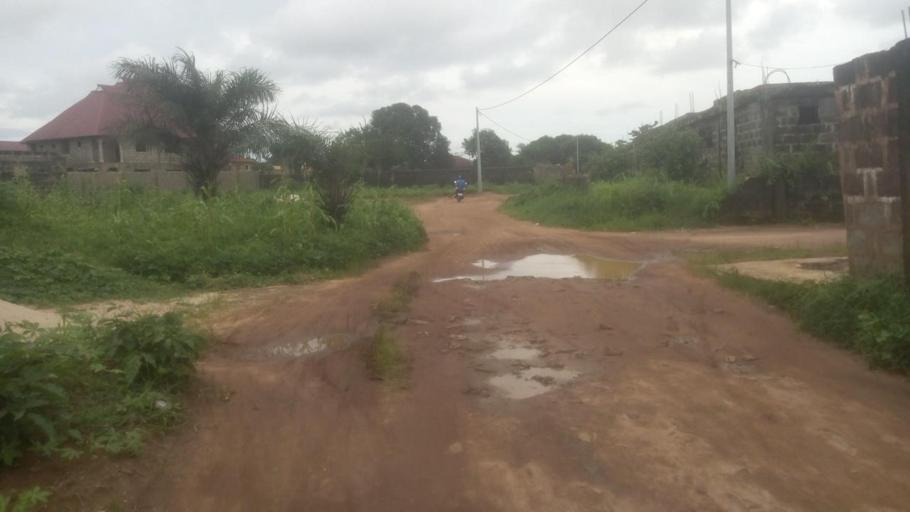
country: SL
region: Northern Province
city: Masoyila
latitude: 8.6032
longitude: -13.1898
